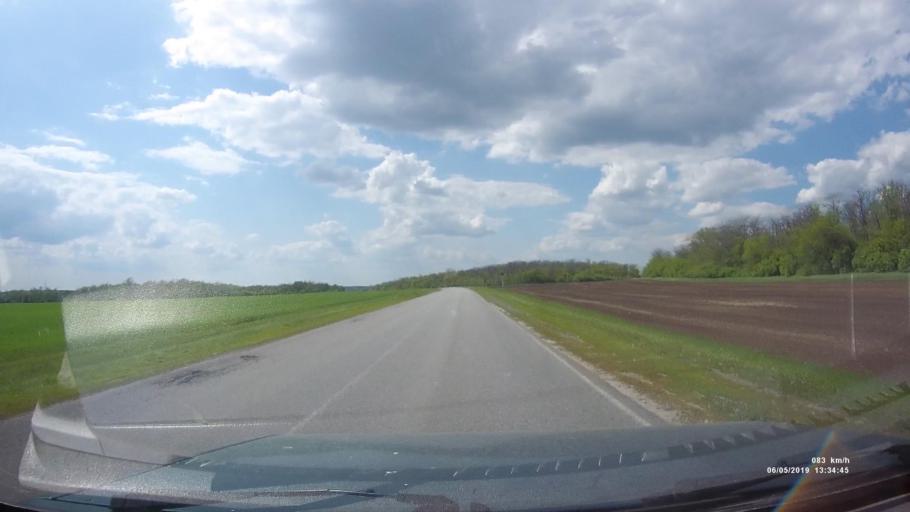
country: RU
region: Rostov
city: Ust'-Donetskiy
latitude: 47.6936
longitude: 40.7576
